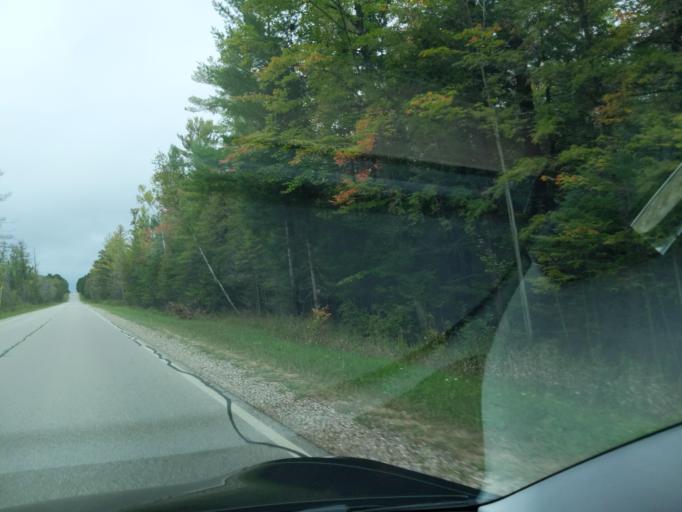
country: US
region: Michigan
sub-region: Grand Traverse County
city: Kingsley
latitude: 44.6152
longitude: -85.3532
